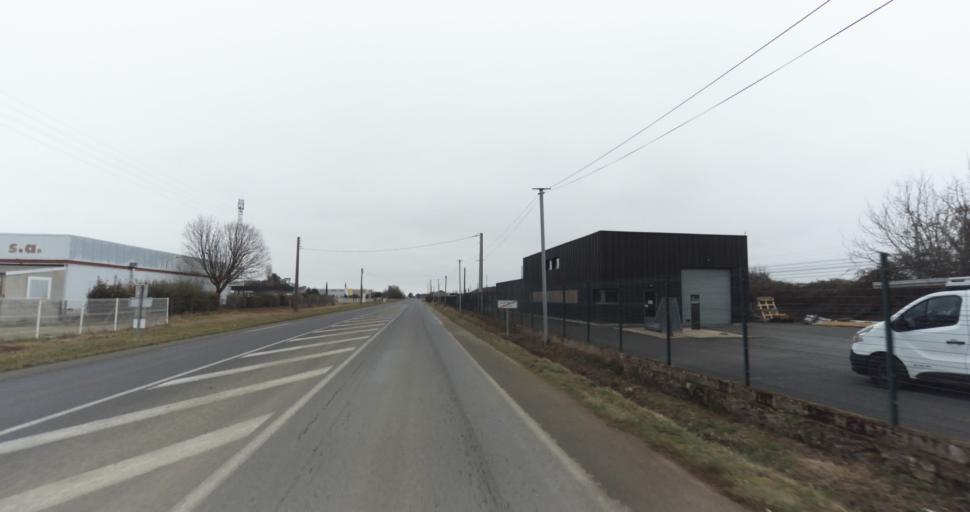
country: FR
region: Pays de la Loire
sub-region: Departement de Maine-et-Loire
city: Montreuil-Bellay
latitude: 47.1235
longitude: -0.1423
